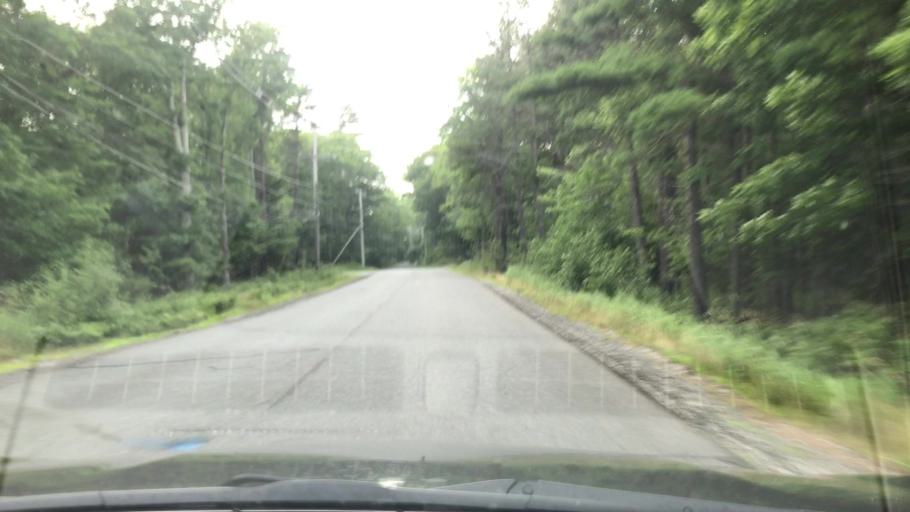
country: US
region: Maine
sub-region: Hancock County
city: Bar Harbor
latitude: 44.3681
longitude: -68.1952
